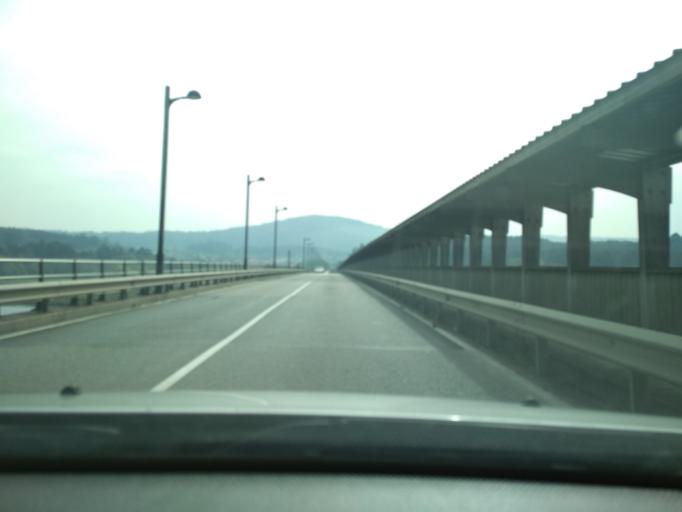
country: ES
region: Galicia
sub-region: Provincia de Pontevedra
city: Catoira
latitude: 42.6770
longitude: -8.7274
